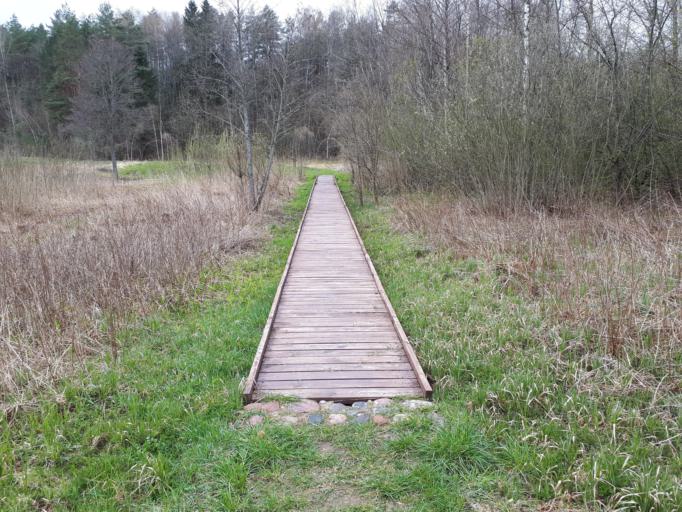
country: LT
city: Aukstadvaris
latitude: 54.5589
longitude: 24.4894
